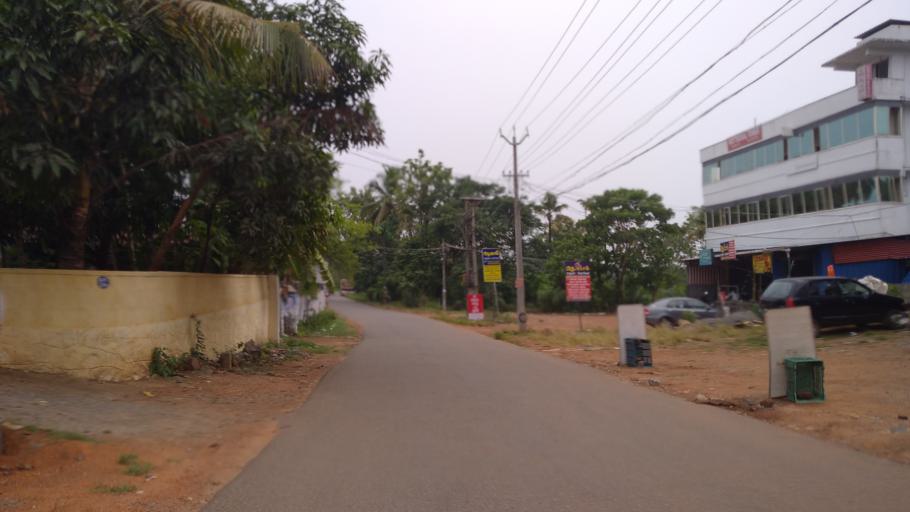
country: IN
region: Kerala
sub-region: Ernakulam
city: Angamali
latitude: 10.1758
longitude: 76.3985
